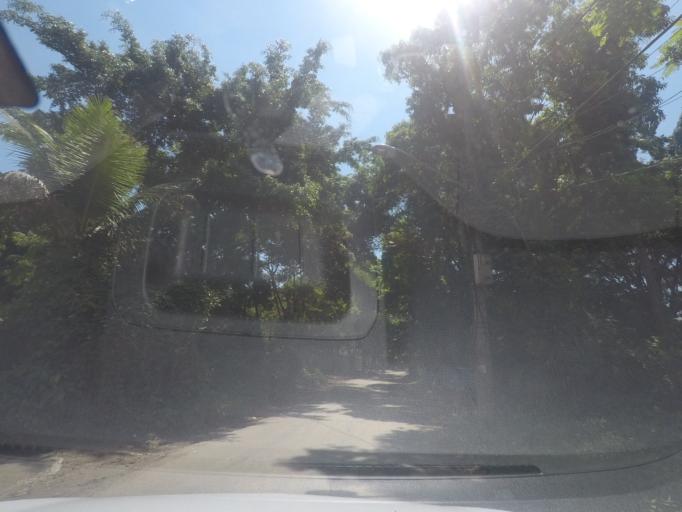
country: BR
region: Rio de Janeiro
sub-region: Nilopolis
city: Nilopolis
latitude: -22.9777
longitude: -43.4527
